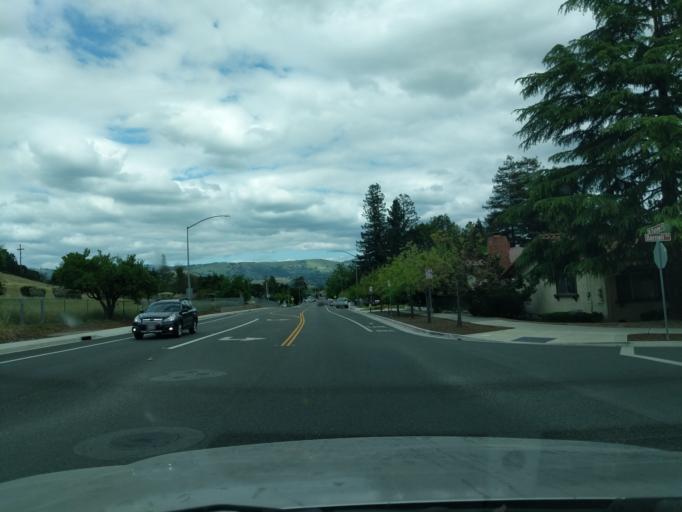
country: US
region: California
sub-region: Santa Clara County
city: Morgan Hill
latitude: 37.1238
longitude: -121.6548
